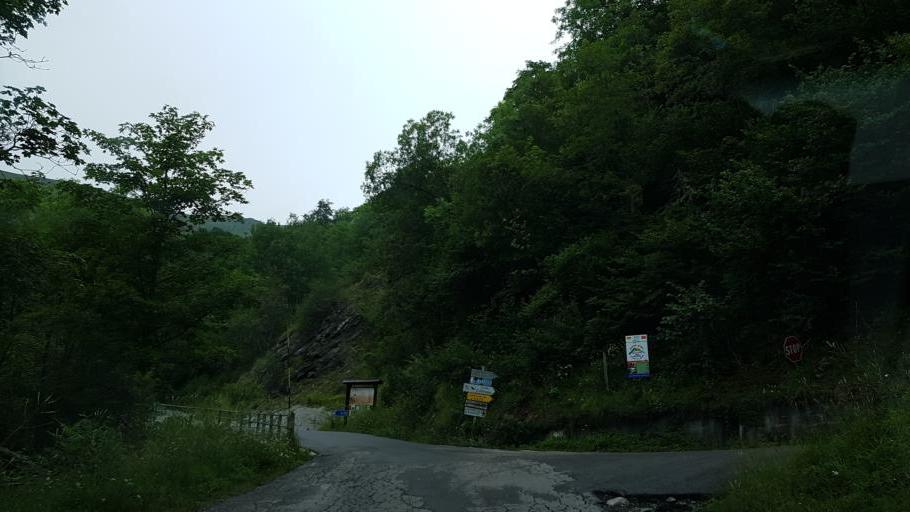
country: IT
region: Piedmont
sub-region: Provincia di Cuneo
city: Stroppo
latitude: 44.5183
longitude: 7.1287
